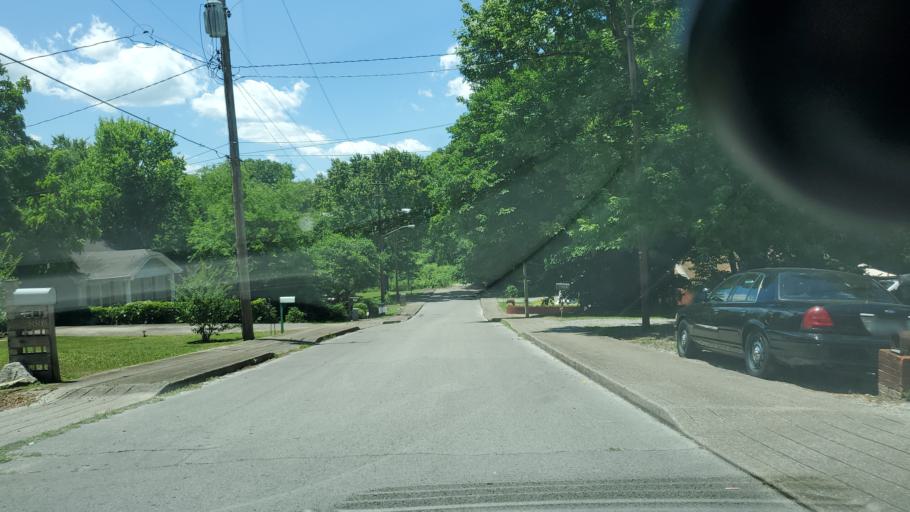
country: US
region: Tennessee
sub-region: Davidson County
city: Nashville
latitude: 36.1907
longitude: -86.7553
